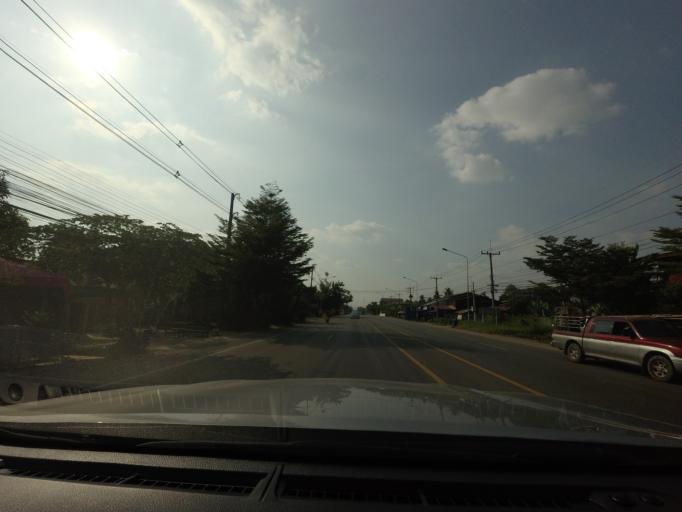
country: TH
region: Sukhothai
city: Ban Na
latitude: 17.0136
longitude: 99.7595
